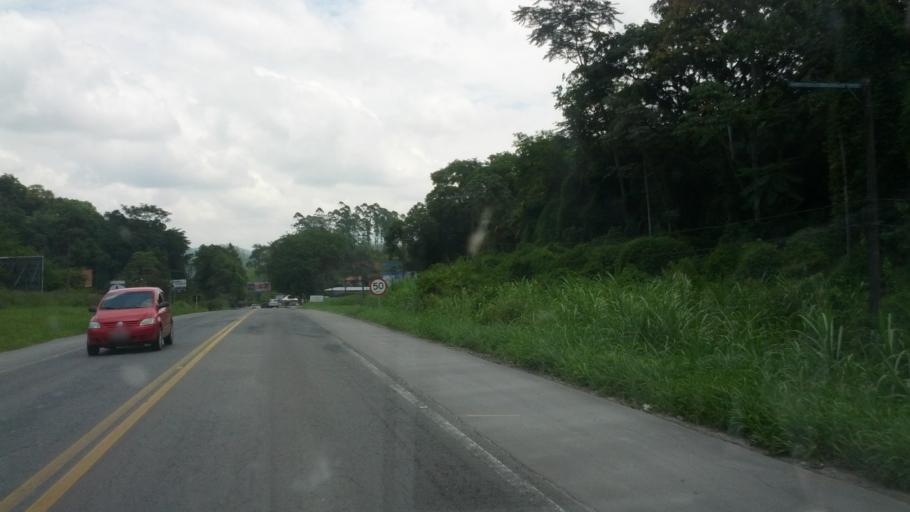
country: BR
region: Santa Catarina
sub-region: Blumenau
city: Blumenau
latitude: -26.8778
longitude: -49.1315
